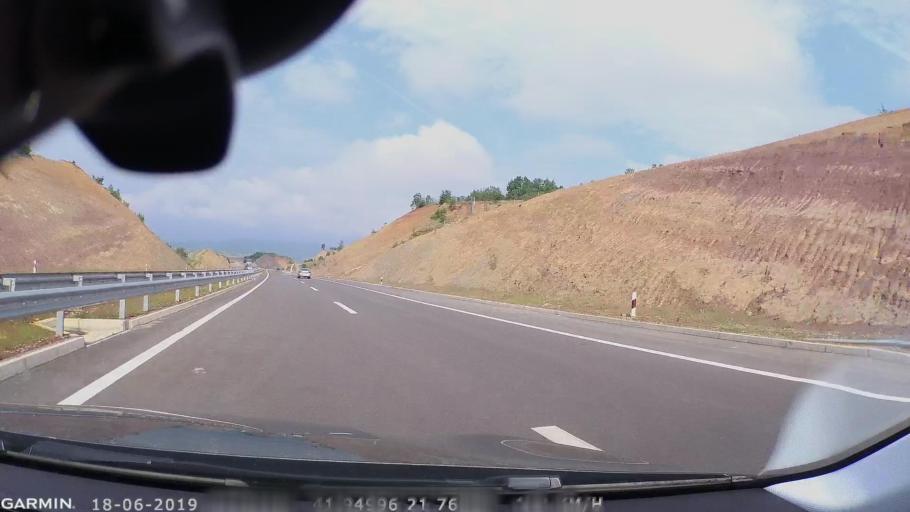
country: MK
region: Sveti Nikole
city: Gorobinci
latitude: 41.9237
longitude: 21.8453
